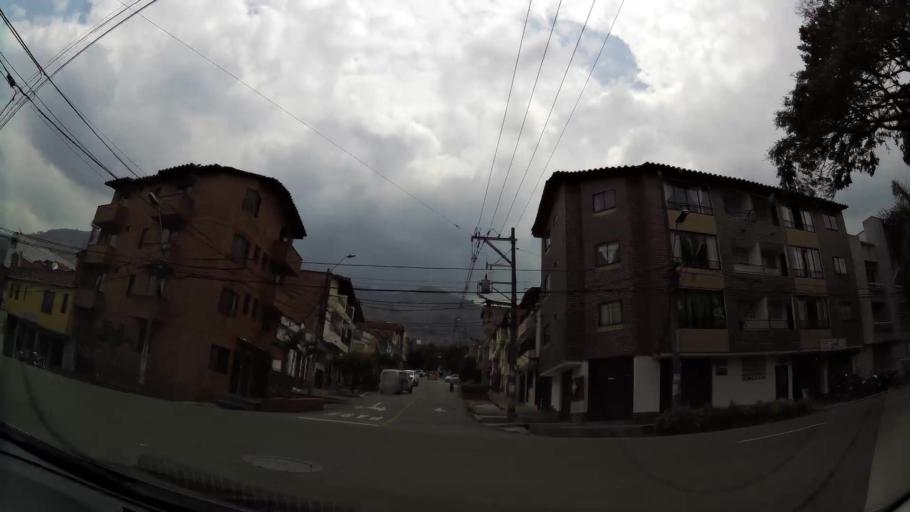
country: CO
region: Antioquia
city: Medellin
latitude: 6.2639
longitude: -75.5565
